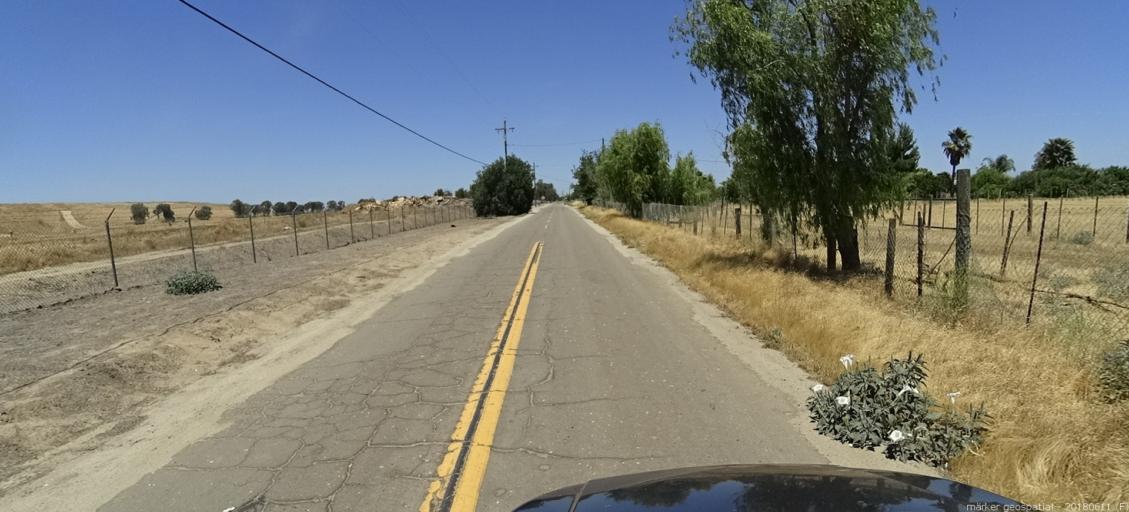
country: US
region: California
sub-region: Madera County
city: Fairmead
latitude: 37.0623
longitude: -120.1934
